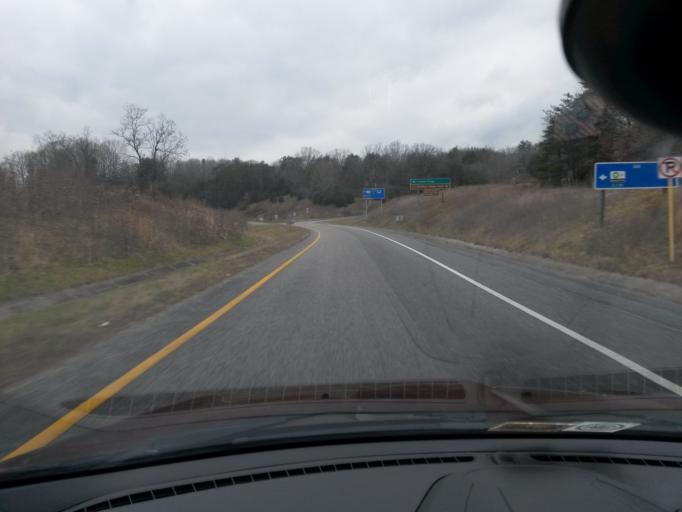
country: US
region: Virginia
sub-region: Alleghany County
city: Clifton Forge
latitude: 37.8274
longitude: -79.7911
